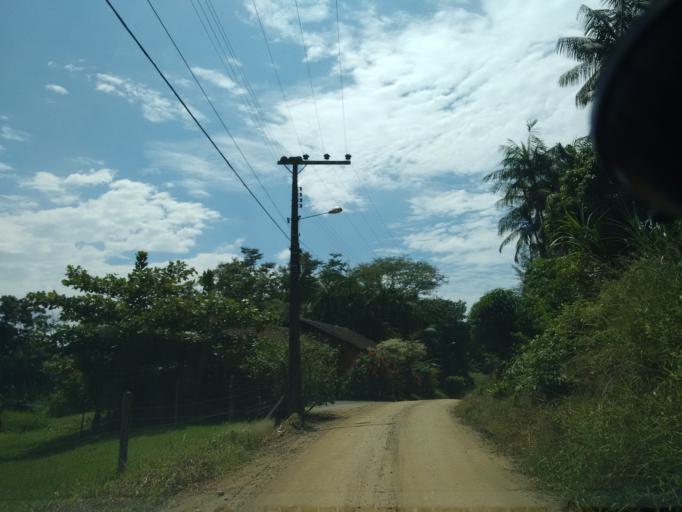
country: BR
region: Santa Catarina
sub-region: Indaial
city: Indaial
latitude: -26.8501
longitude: -49.1632
